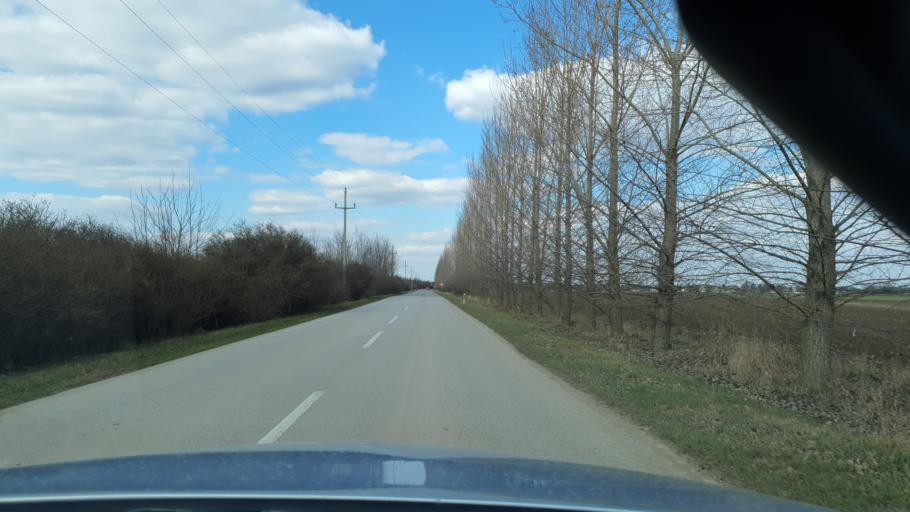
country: RS
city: Ravno Selo
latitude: 45.4376
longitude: 19.6063
